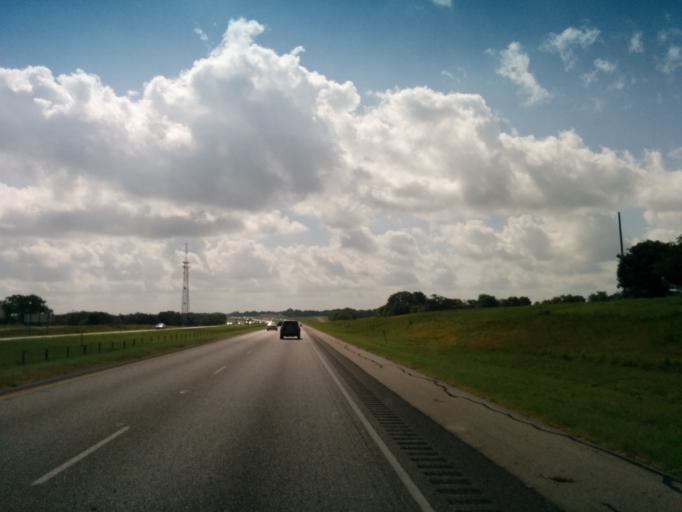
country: US
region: Texas
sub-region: Fayette County
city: Flatonia
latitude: 29.6930
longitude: -97.0170
